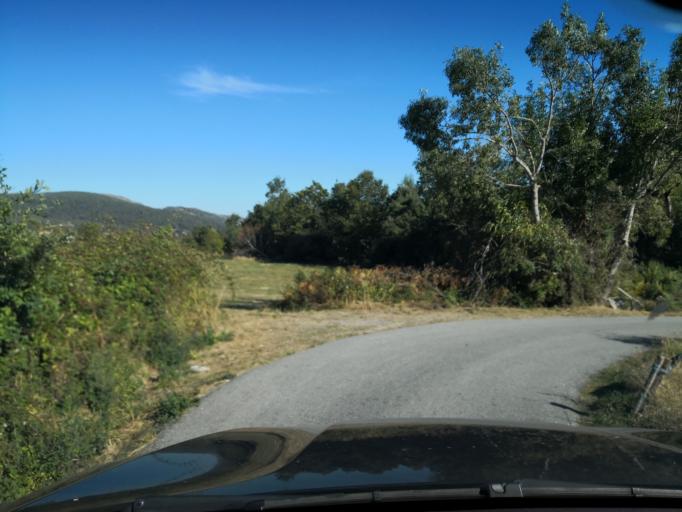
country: PT
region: Vila Real
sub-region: Santa Marta de Penaguiao
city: Santa Marta de Penaguiao
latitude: 41.2883
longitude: -7.8819
